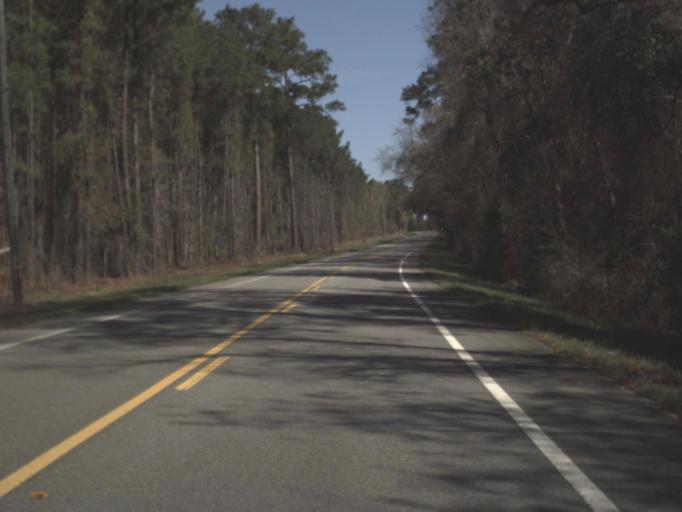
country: US
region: Florida
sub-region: Jefferson County
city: Monticello
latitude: 30.4952
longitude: -84.0259
